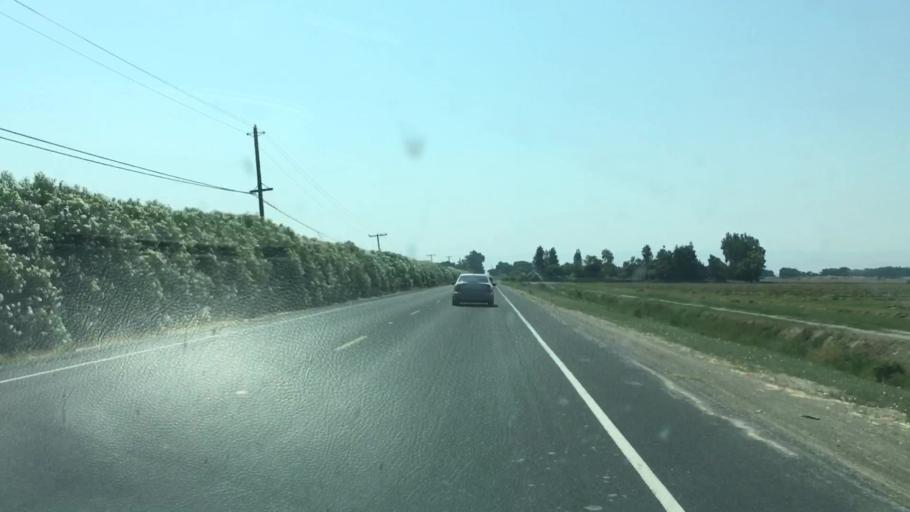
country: US
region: California
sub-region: San Joaquin County
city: Tracy
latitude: 37.8144
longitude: -121.4499
